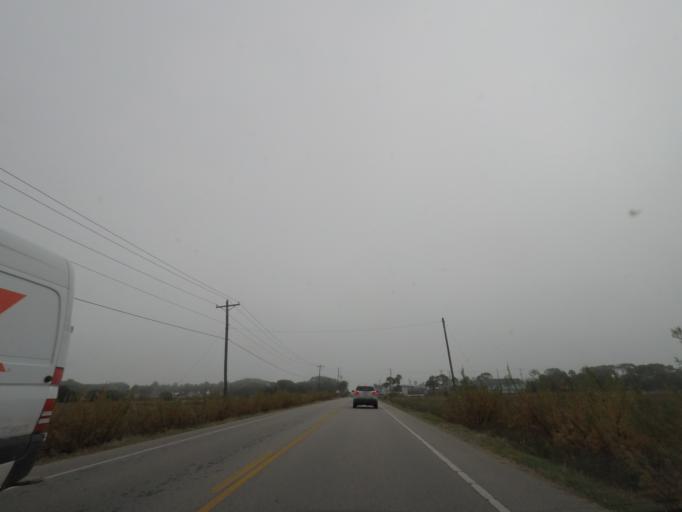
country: US
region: South Carolina
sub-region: Charleston County
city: Seabrook Island
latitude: 32.5060
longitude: -80.2980
